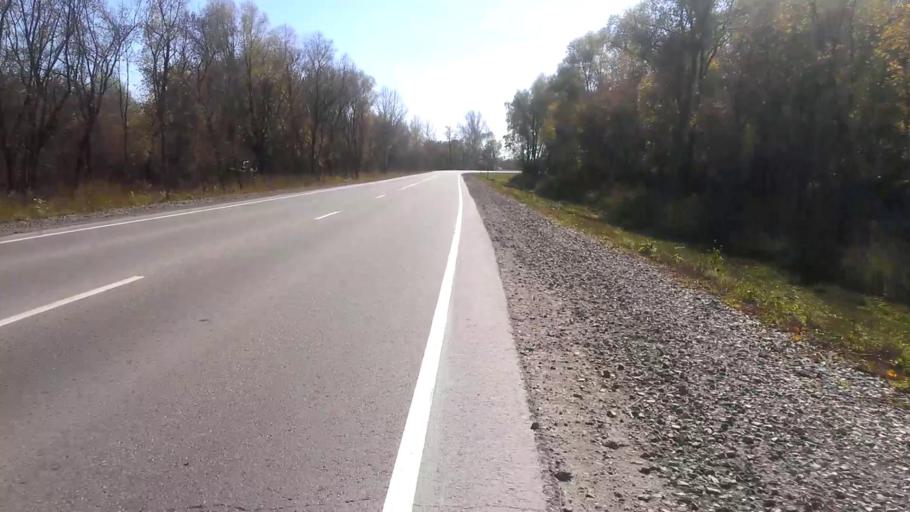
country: RU
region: Altai Krai
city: Sannikovo
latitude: 53.3253
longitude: 83.9422
